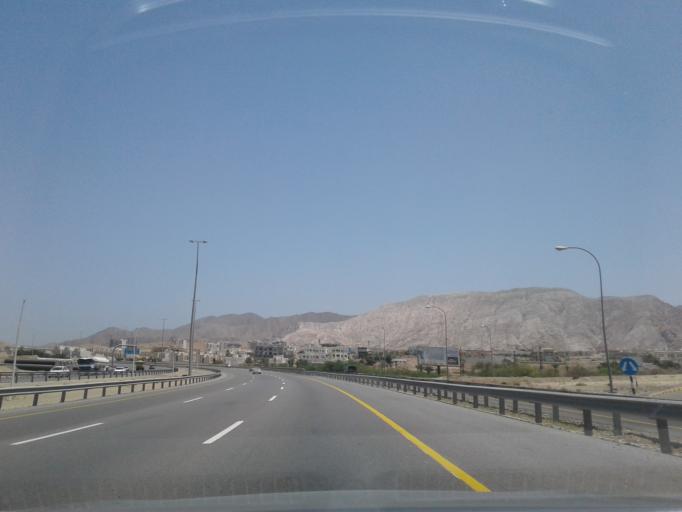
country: OM
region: Muhafazat Masqat
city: Bawshar
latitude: 23.5635
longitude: 58.3878
